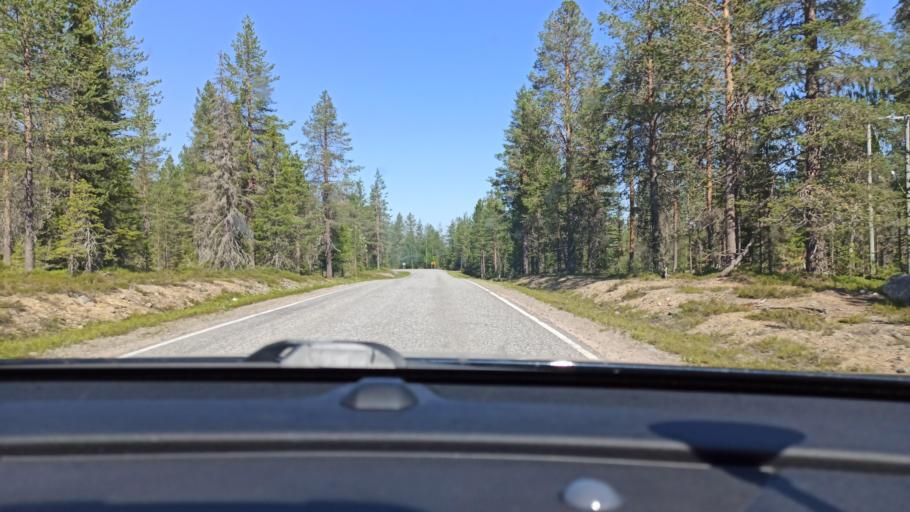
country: FI
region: Lapland
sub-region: Tunturi-Lappi
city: Kolari
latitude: 67.6808
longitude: 24.1381
